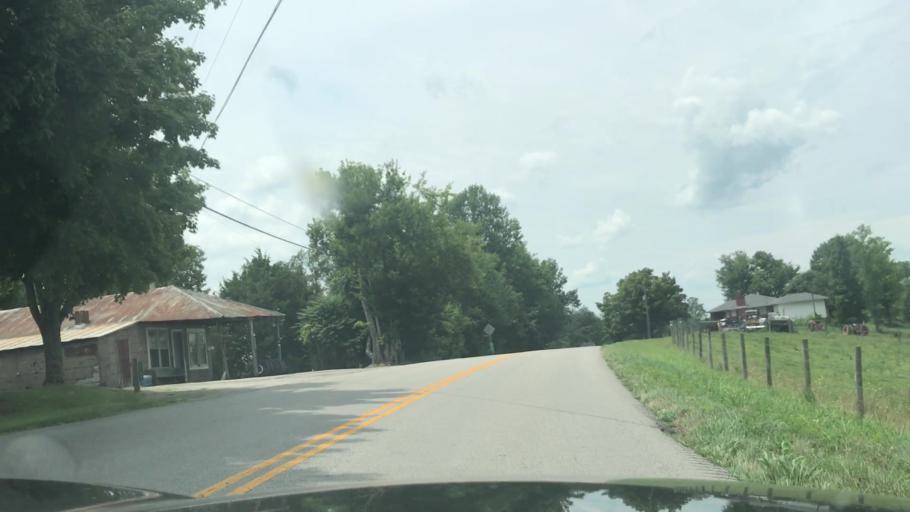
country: US
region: Kentucky
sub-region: Green County
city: Greensburg
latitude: 37.2716
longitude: -85.5293
